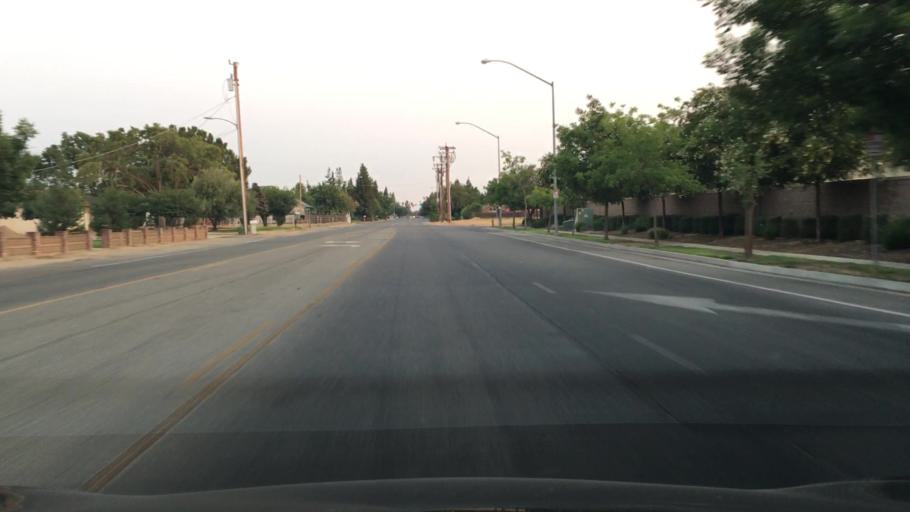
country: US
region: California
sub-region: Fresno County
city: Clovis
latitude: 36.8632
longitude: -119.7478
